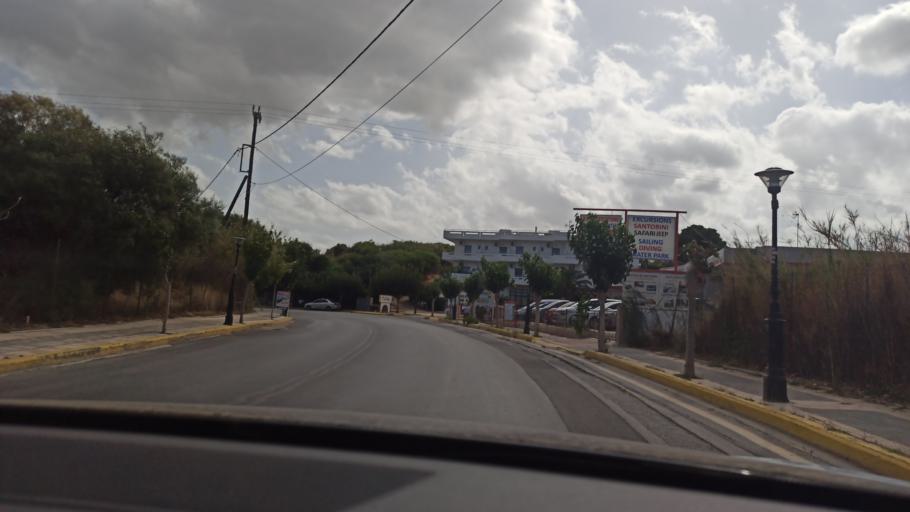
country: GR
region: Crete
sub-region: Nomos Irakleiou
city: Gazi
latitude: 35.3355
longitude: 25.0571
